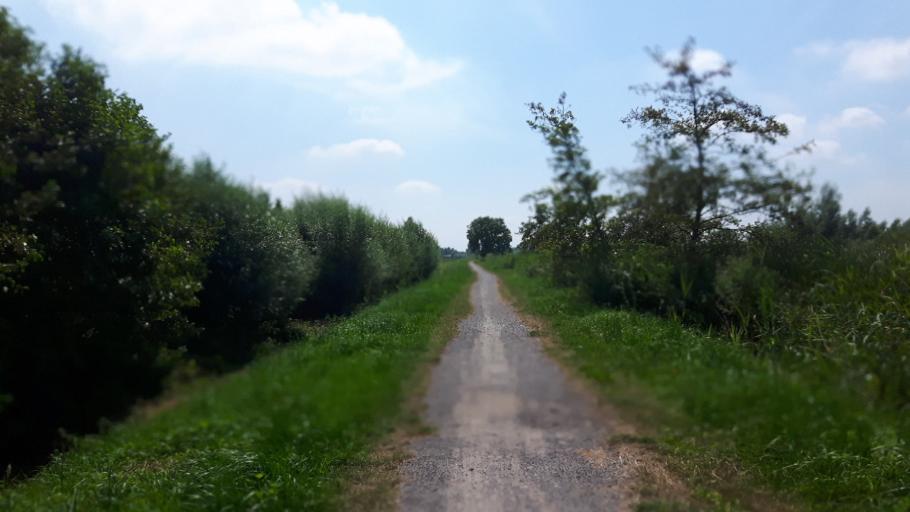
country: NL
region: Utrecht
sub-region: Gemeente Lopik
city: Lopik
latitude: 51.9310
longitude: 5.0003
